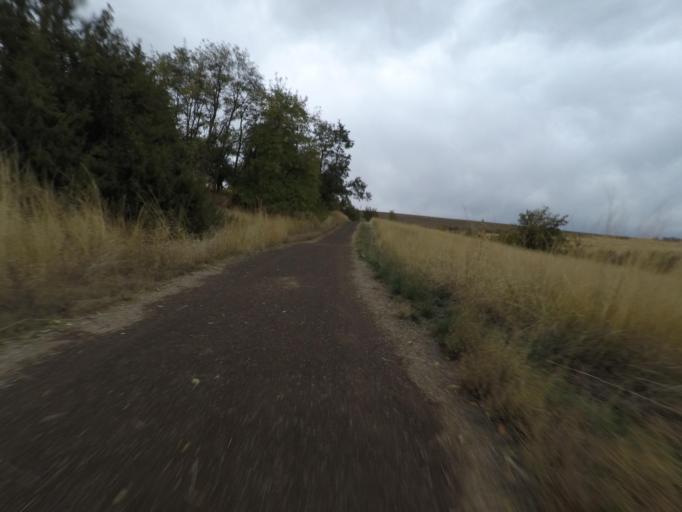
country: US
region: Washington
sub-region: Walla Walla County
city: Walla Walla East
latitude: 46.0617
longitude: -118.2565
